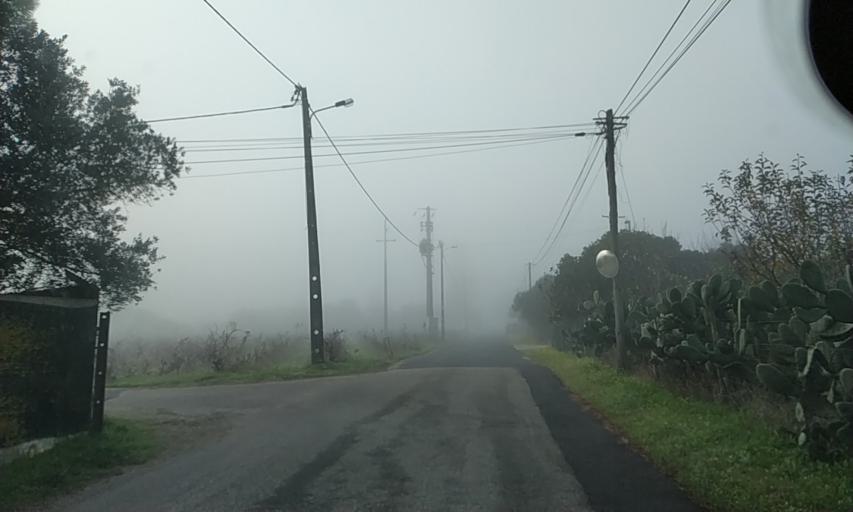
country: PT
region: Setubal
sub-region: Palmela
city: Pinhal Novo
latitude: 38.6081
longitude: -8.8850
